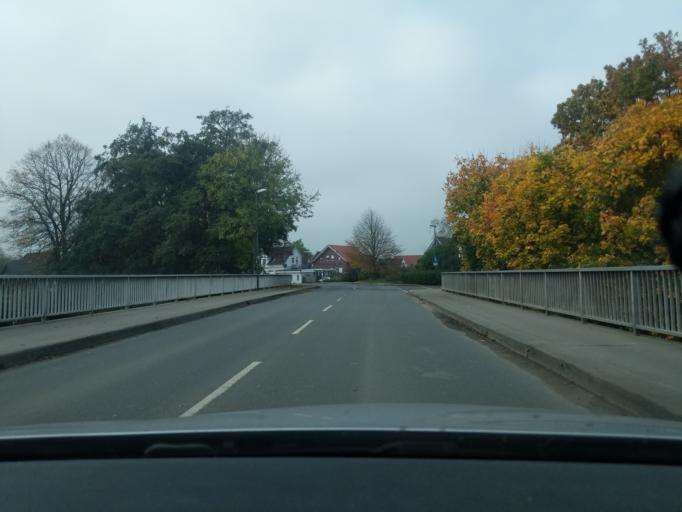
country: DE
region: Lower Saxony
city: Otterndorf
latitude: 53.8108
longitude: 8.8963
